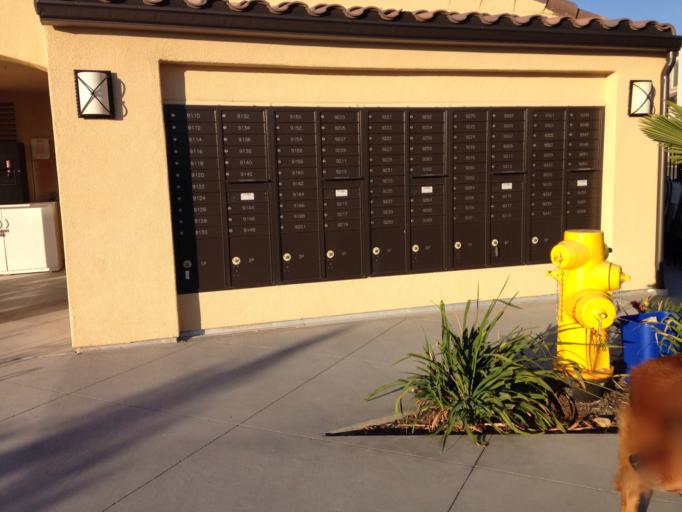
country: US
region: California
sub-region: San Luis Obispo County
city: Atascadero
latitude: 35.4560
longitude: -120.6301
